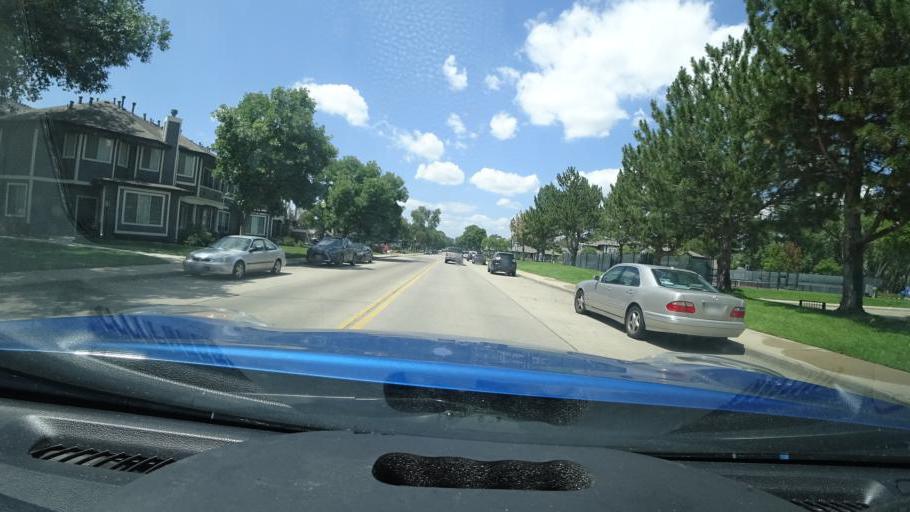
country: US
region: Colorado
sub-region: Arapahoe County
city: Glendale
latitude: 39.6979
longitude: -104.8831
